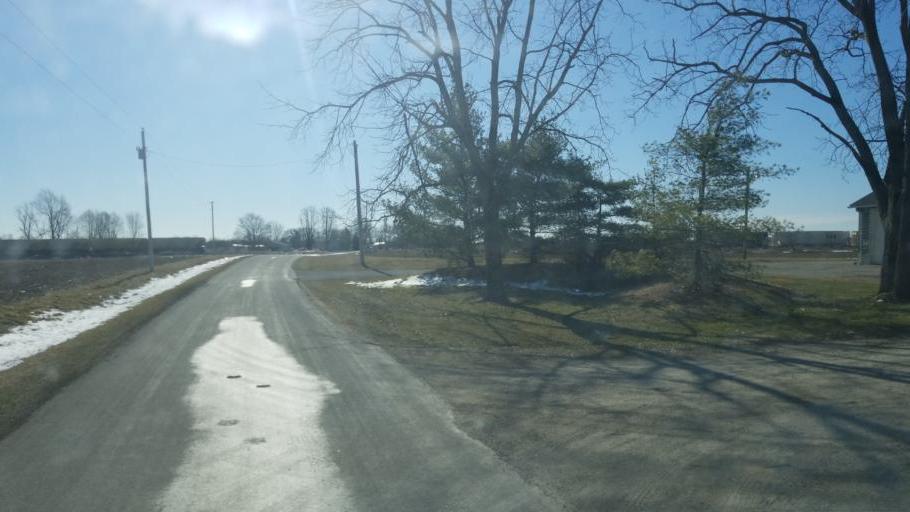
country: US
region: Ohio
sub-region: Morrow County
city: Mount Gilead
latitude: 40.6643
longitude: -82.9229
